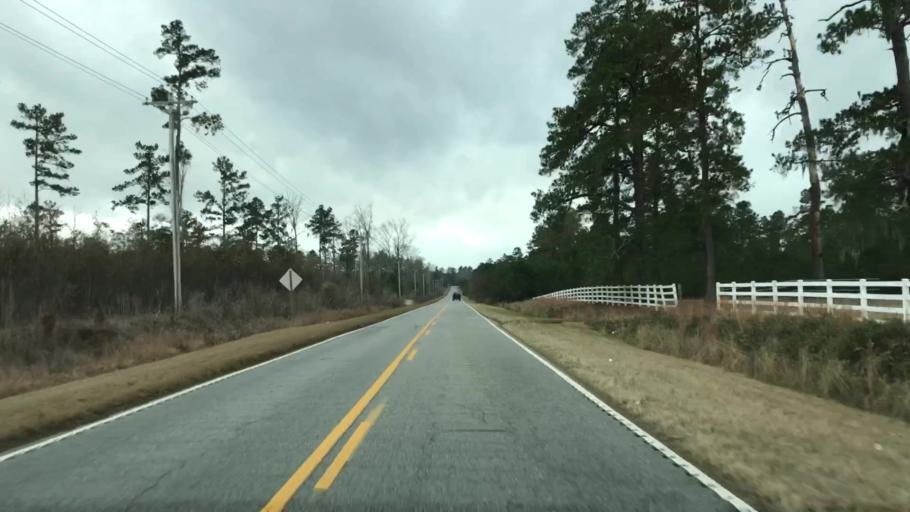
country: US
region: South Carolina
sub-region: Florence County
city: Johnsonville
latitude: 33.6473
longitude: -79.4204
